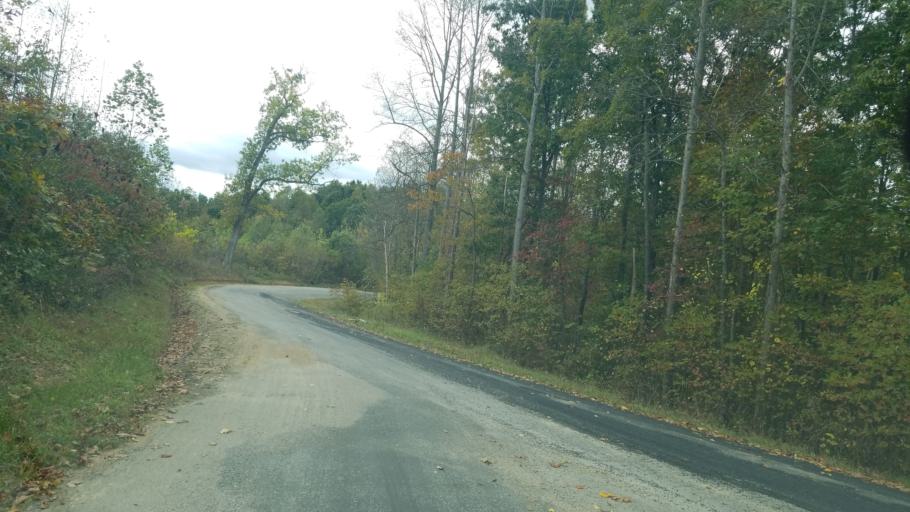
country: US
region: Ohio
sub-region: Jackson County
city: Wellston
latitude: 39.1601
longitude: -82.5919
